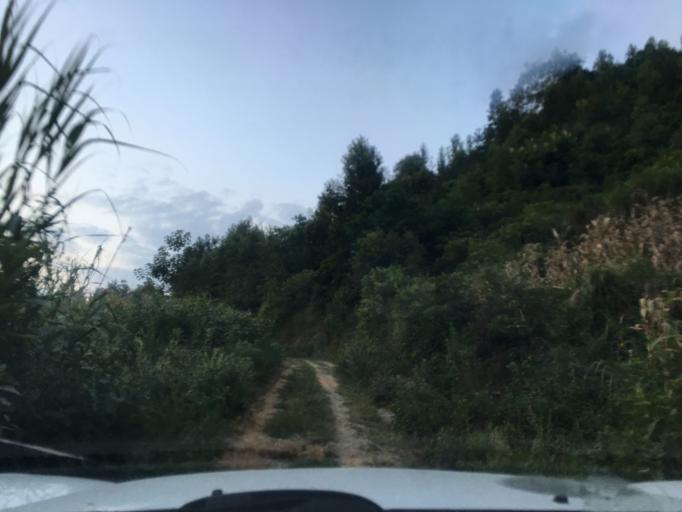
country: CN
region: Guangxi Zhuangzu Zizhiqu
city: Xinzhou
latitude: 25.3518
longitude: 105.7417
